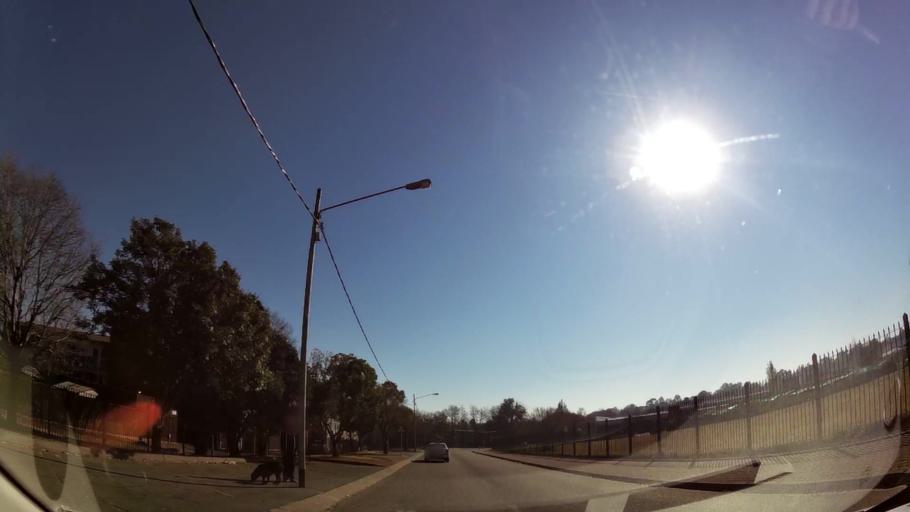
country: ZA
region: Gauteng
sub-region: City of Tshwane Metropolitan Municipality
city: Centurion
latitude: -25.8570
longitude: 28.2151
